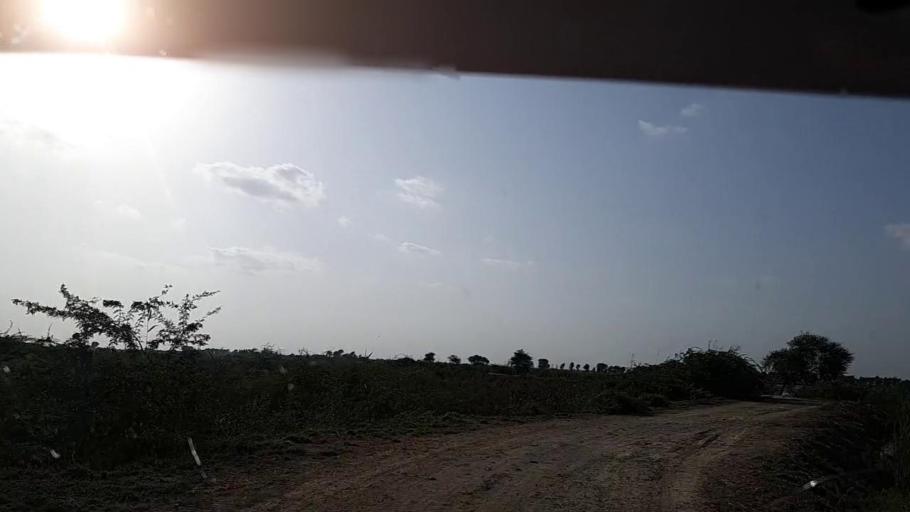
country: PK
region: Sindh
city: Badin
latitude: 24.5582
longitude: 68.8907
